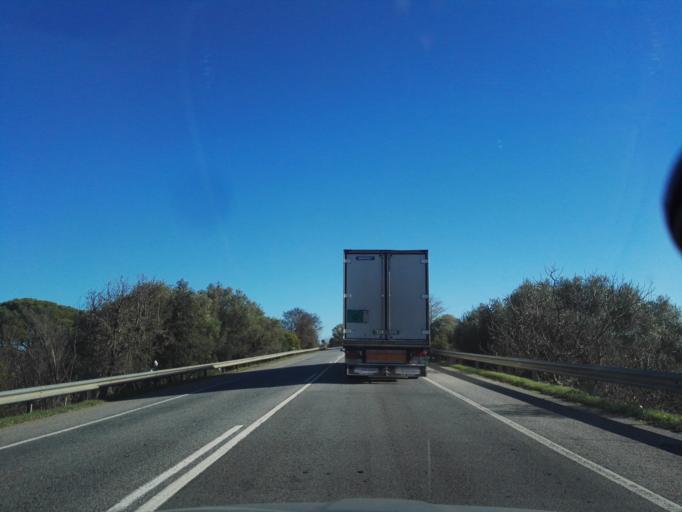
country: PT
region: Evora
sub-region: Estremoz
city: Estremoz
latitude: 38.8343
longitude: -7.5621
